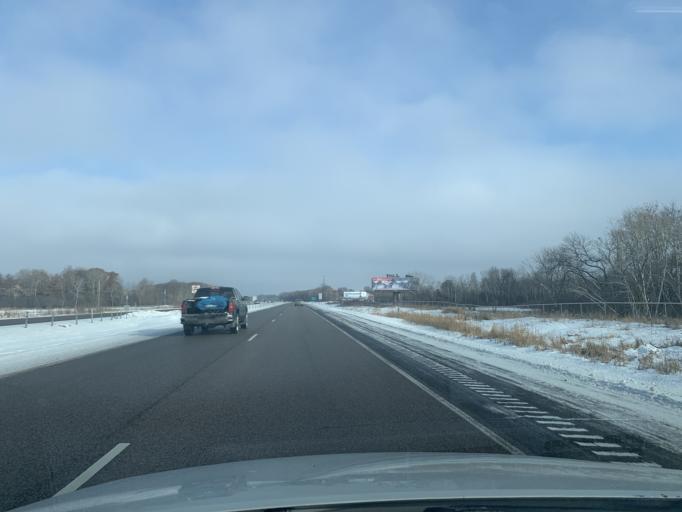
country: US
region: Minnesota
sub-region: Chisago County
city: Wyoming
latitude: 45.3440
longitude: -93.0026
